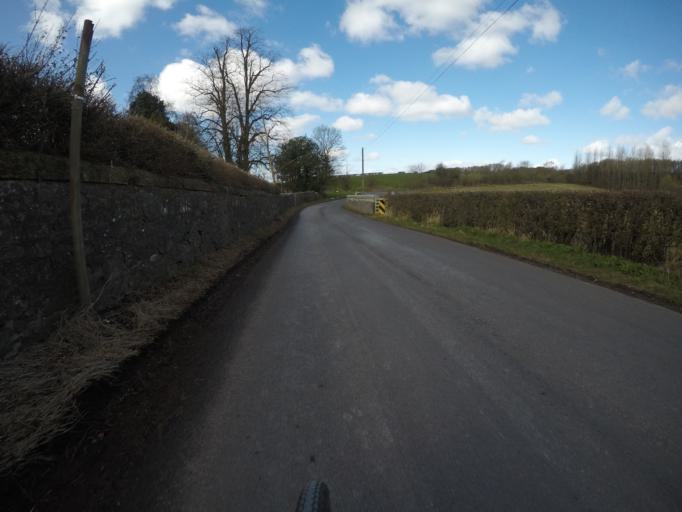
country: GB
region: Scotland
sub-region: East Ayrshire
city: Crosshouse
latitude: 55.6032
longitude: -4.5730
